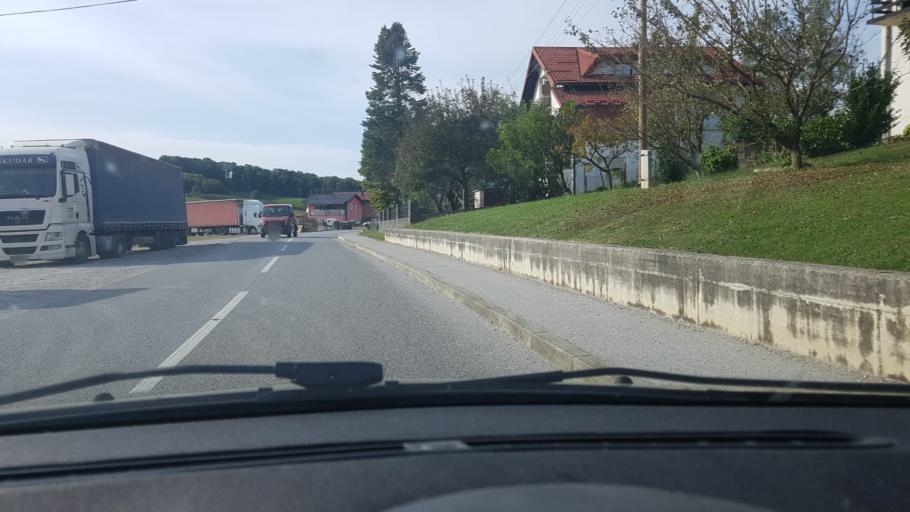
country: HR
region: Krapinsko-Zagorska
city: Mihovljan
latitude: 46.1350
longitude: 15.9687
